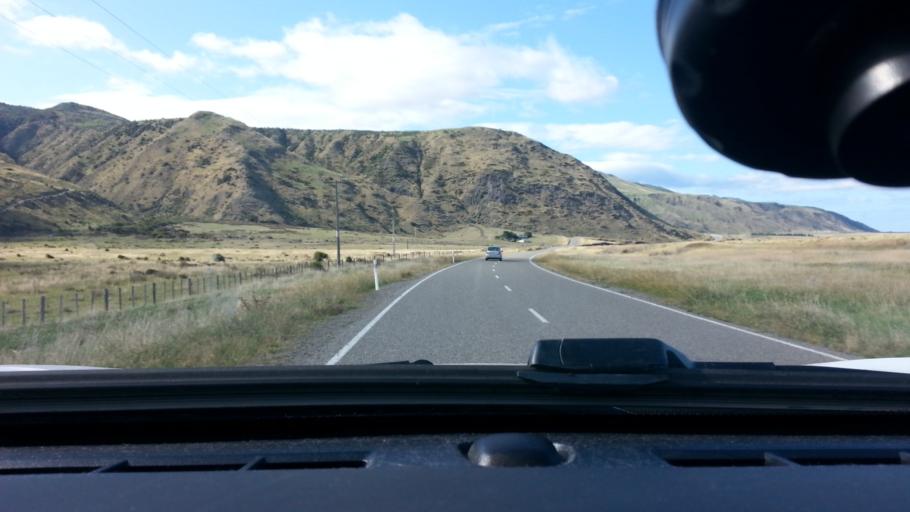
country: NZ
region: Wellington
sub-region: South Wairarapa District
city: Waipawa
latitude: -41.5349
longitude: 175.2133
